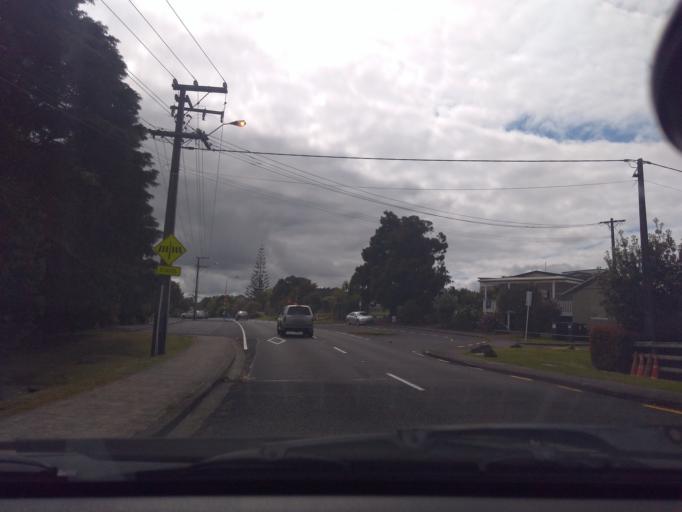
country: NZ
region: Auckland
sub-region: Auckland
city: Muriwai Beach
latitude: -36.8520
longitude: 174.5389
